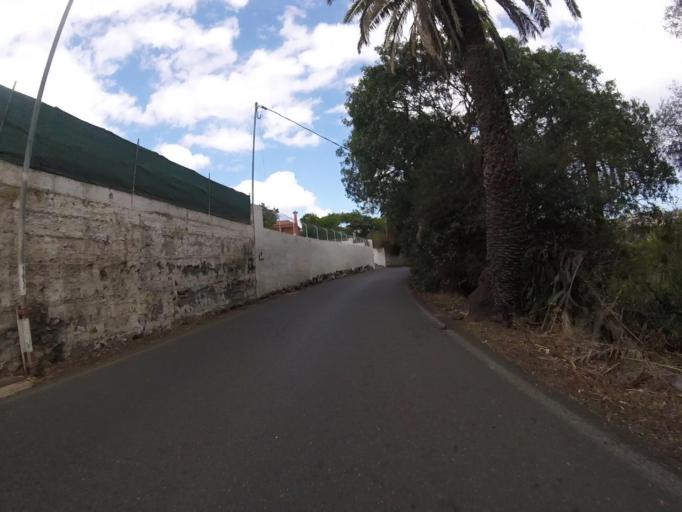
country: ES
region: Canary Islands
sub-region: Provincia de Las Palmas
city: Santa Brigida
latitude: 28.0434
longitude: -15.4887
